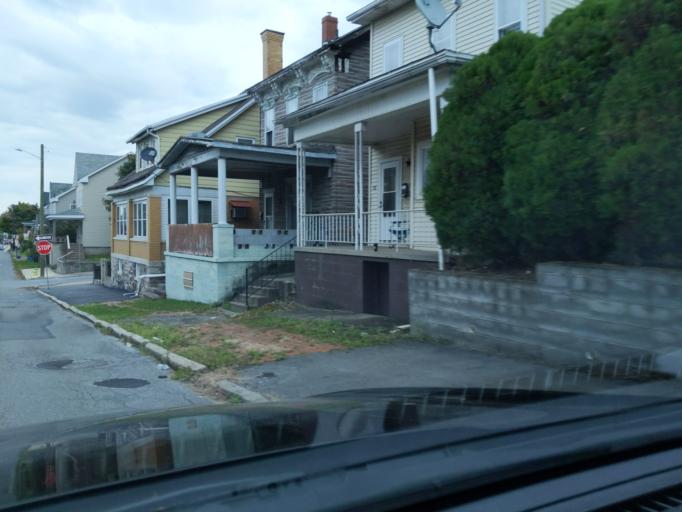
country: US
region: Pennsylvania
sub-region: Blair County
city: Altoona
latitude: 40.5148
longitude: -78.3886
